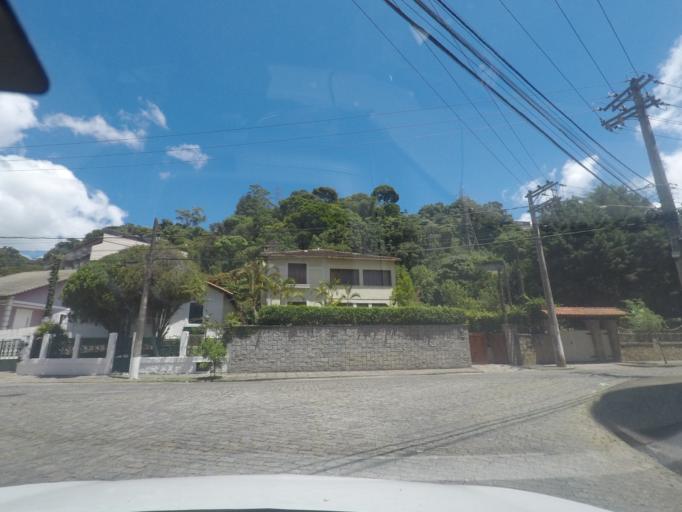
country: BR
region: Rio de Janeiro
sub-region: Teresopolis
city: Teresopolis
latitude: -22.4207
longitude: -42.9796
